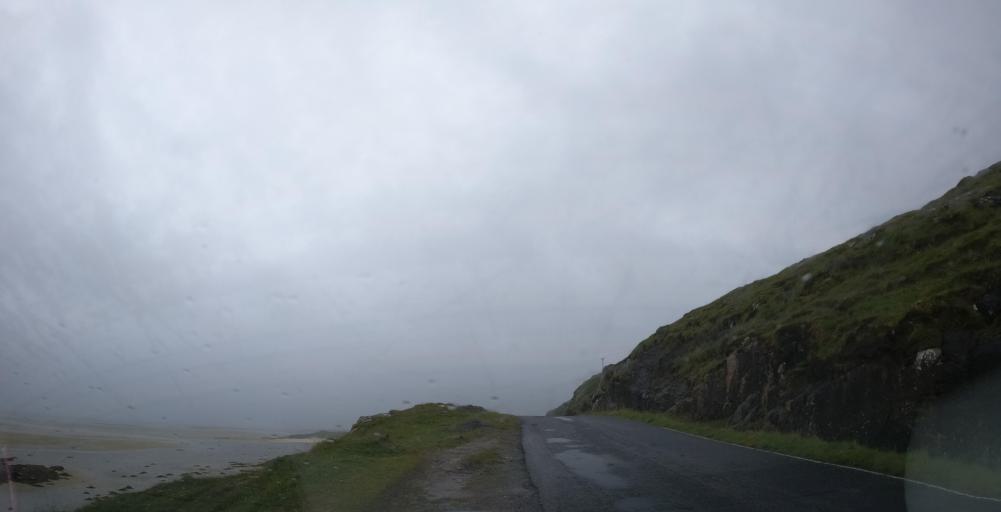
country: GB
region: Scotland
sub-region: Eilean Siar
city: Barra
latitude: 57.0175
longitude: -7.4370
